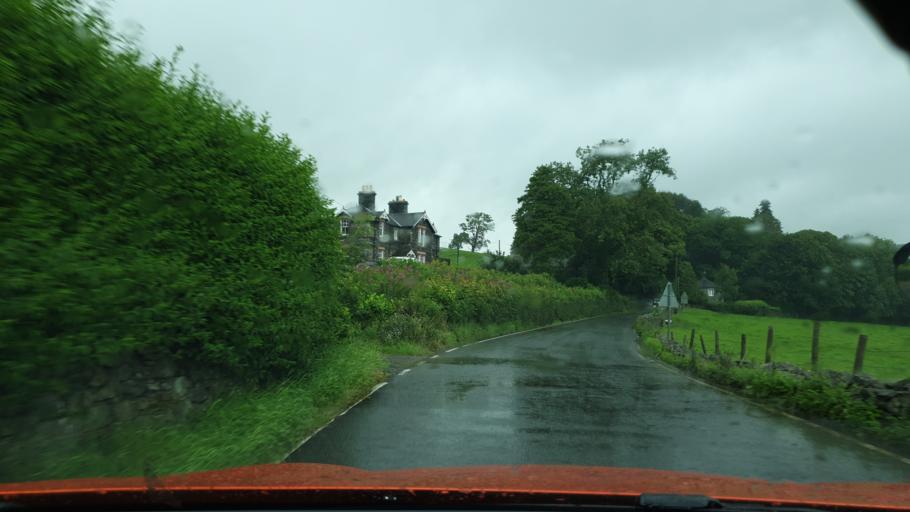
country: GB
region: England
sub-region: Cumbria
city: Ulverston
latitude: 54.2491
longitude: -3.0683
